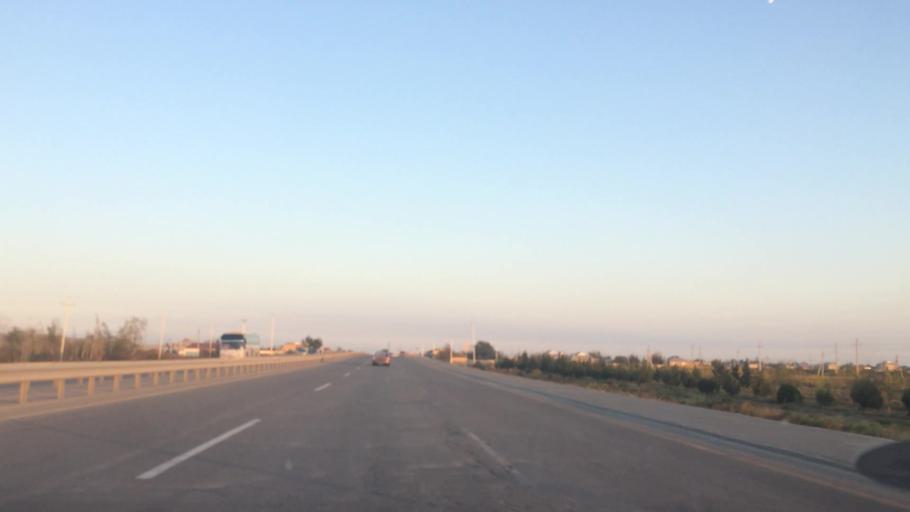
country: AZ
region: Baki
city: Qobustan
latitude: 39.9746
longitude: 49.2525
